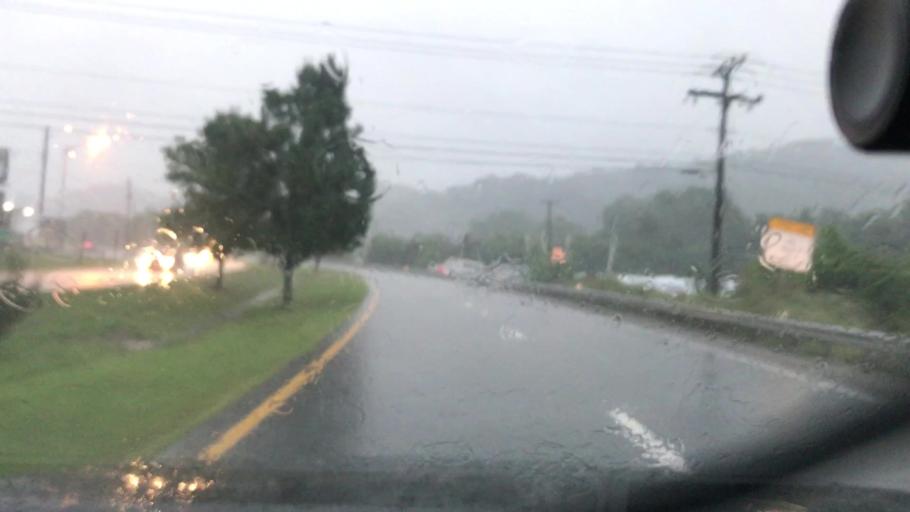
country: US
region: Virginia
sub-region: Giles County
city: Narrows
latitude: 37.3344
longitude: -80.8043
